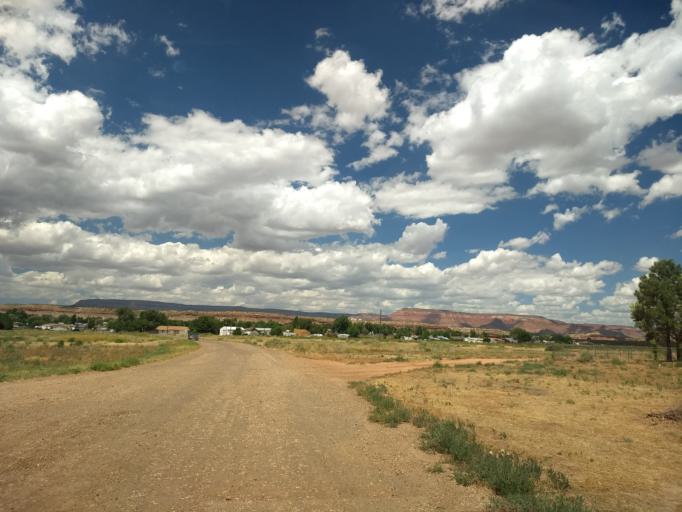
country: US
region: Arizona
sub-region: Coconino County
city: Fredonia
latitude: 36.9447
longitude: -112.5149
